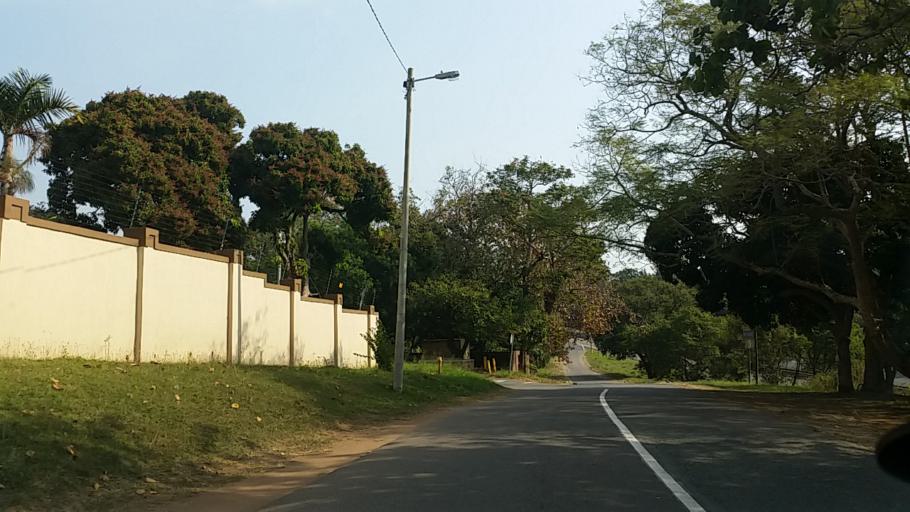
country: ZA
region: KwaZulu-Natal
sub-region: eThekwini Metropolitan Municipality
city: Berea
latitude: -29.8327
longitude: 30.9313
